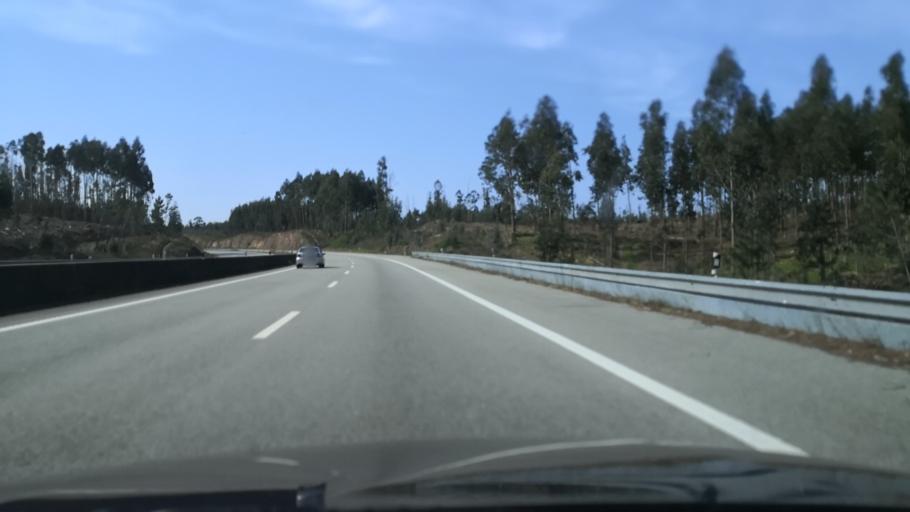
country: PT
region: Aveiro
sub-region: Agueda
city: Valongo
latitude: 40.6674
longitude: -8.4043
